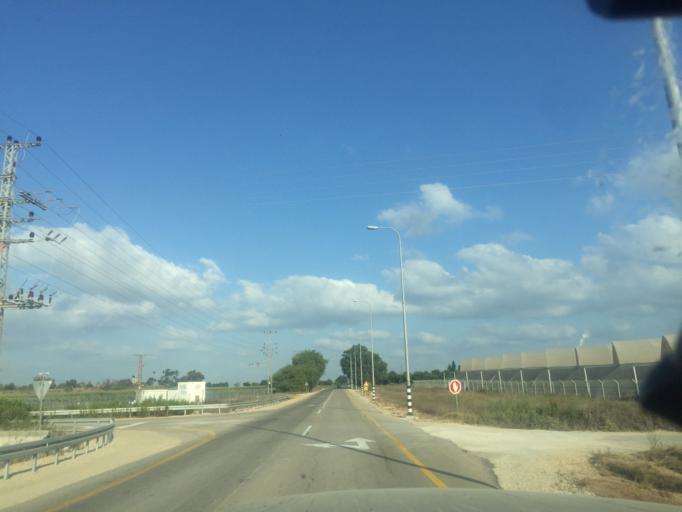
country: PS
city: Umm an Nasr
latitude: 31.6070
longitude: 34.5523
